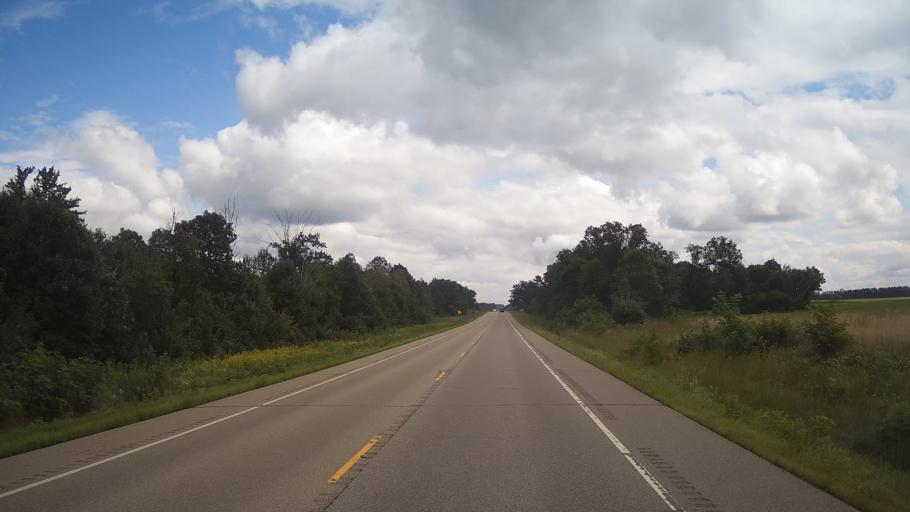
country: US
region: Wisconsin
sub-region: Adams County
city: Friendship
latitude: 44.0220
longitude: -89.6460
